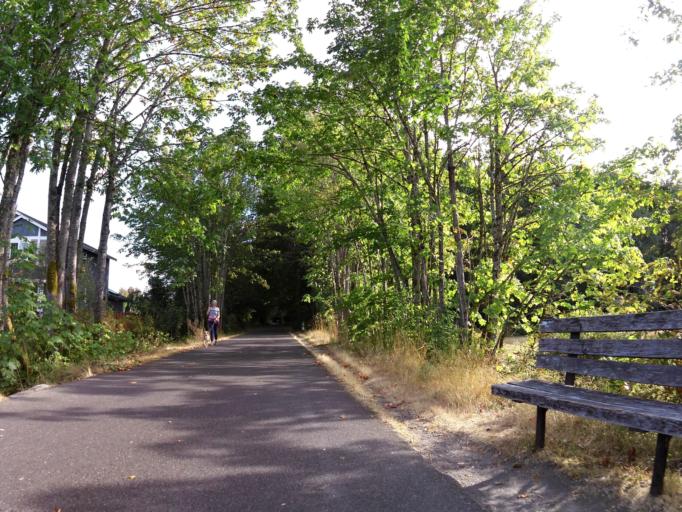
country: US
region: Washington
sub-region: Thurston County
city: Lacey
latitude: 47.0111
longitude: -122.8337
